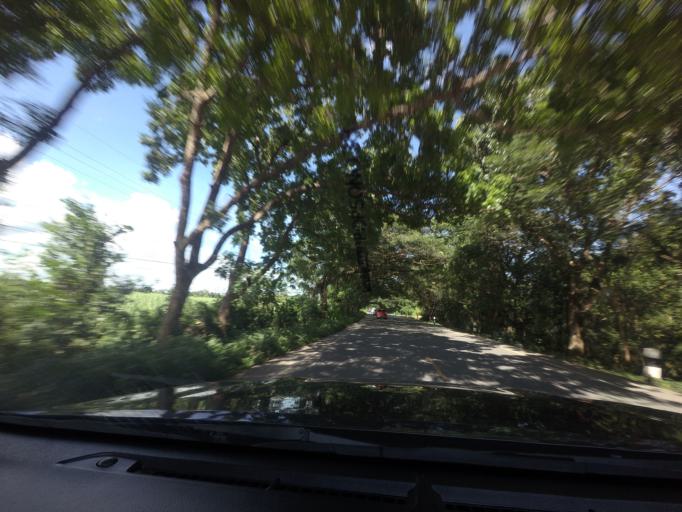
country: TH
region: Kanchanaburi
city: Phanom Thuan
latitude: 14.1697
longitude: 99.8392
